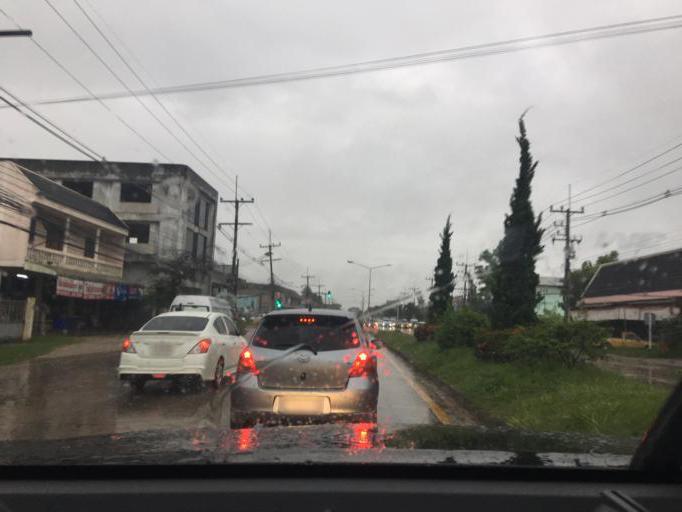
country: TH
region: Chiang Rai
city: Chiang Rai
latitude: 20.0053
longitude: 99.8674
